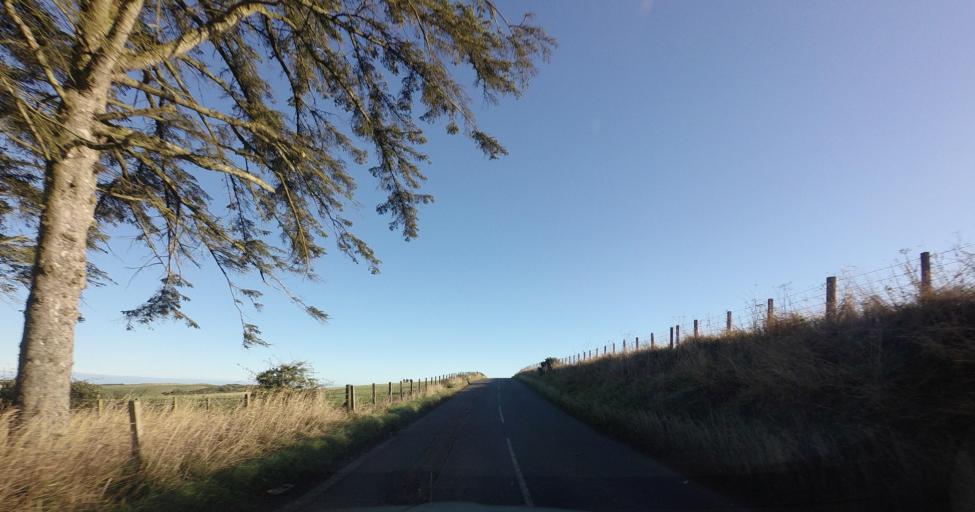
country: GB
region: Scotland
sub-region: Aberdeenshire
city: Rosehearty
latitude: 57.6729
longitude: -2.2988
